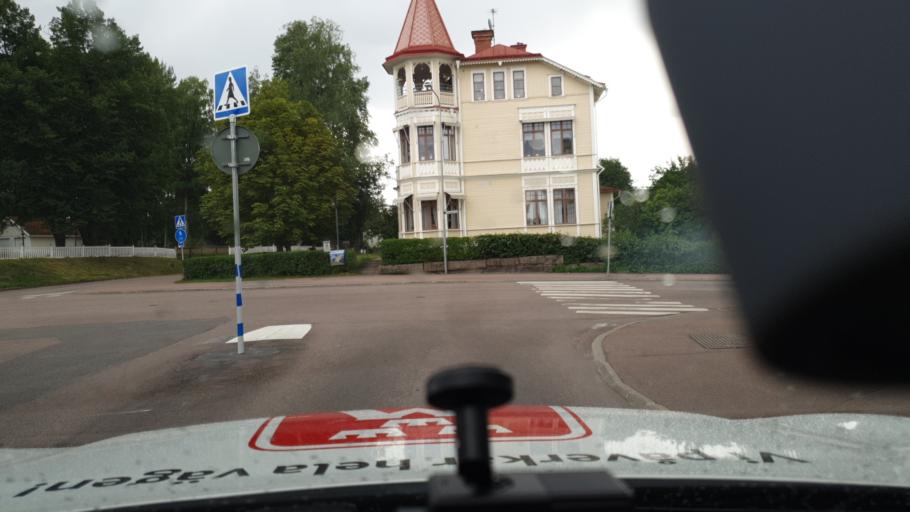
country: SE
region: Vaermland
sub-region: Sunne Kommun
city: Sunne
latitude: 59.8363
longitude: 13.1417
